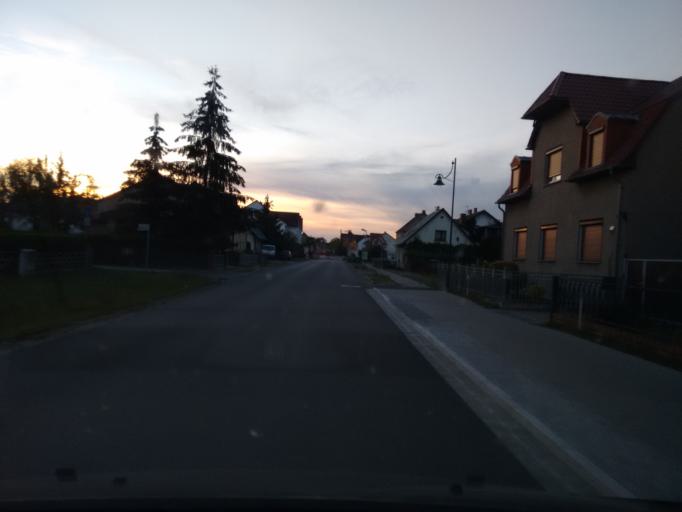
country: DE
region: Brandenburg
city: Storkow
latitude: 52.2495
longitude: 13.9311
